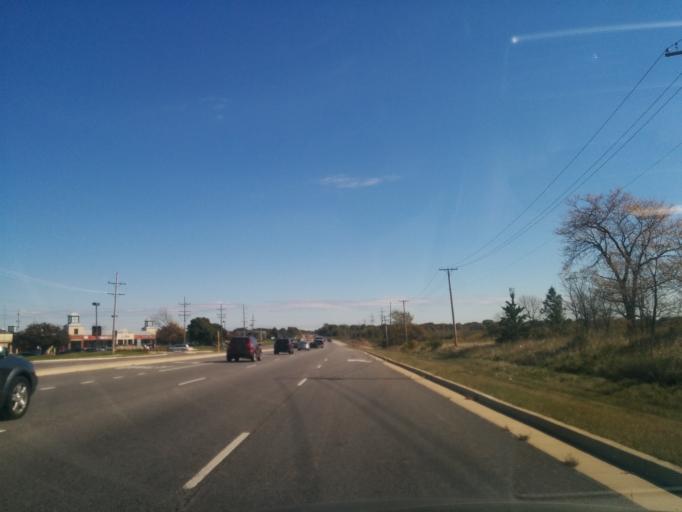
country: US
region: Illinois
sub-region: DuPage County
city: Wheaton
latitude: 41.8288
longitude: -88.1031
